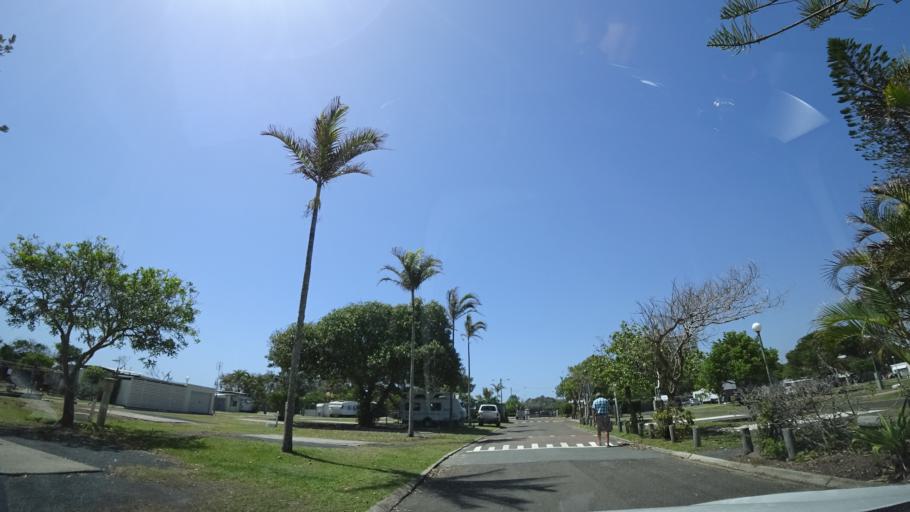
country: AU
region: Queensland
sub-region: Sunshine Coast
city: Mooloolaba
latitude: -26.6525
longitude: 153.1016
